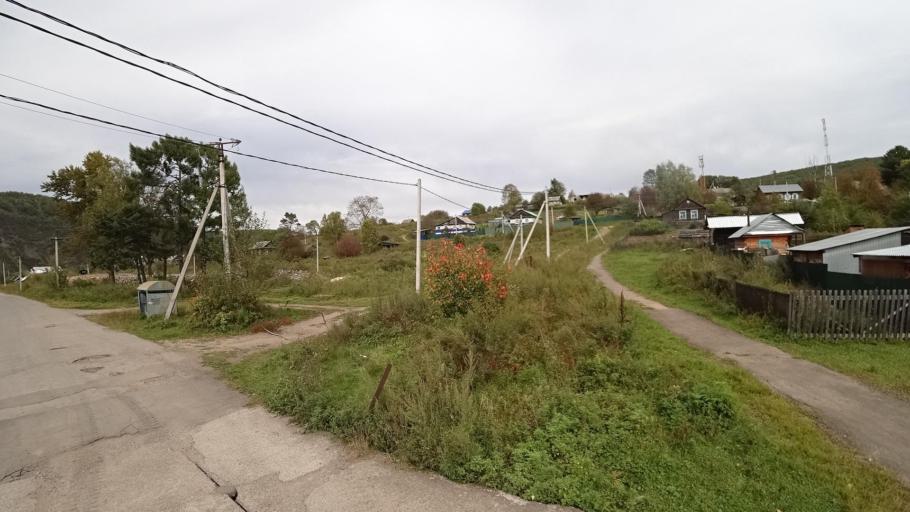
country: RU
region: Jewish Autonomous Oblast
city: Khingansk
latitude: 49.1263
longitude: 131.2016
